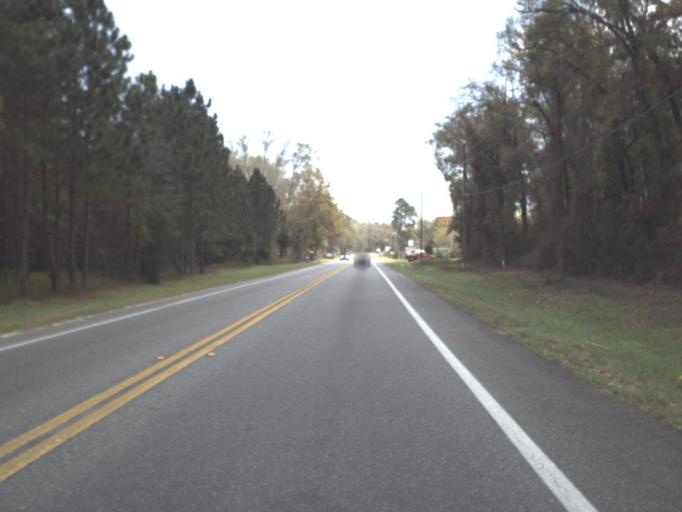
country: US
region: Florida
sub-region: Wakulla County
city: Crawfordville
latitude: 30.1260
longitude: -84.3866
